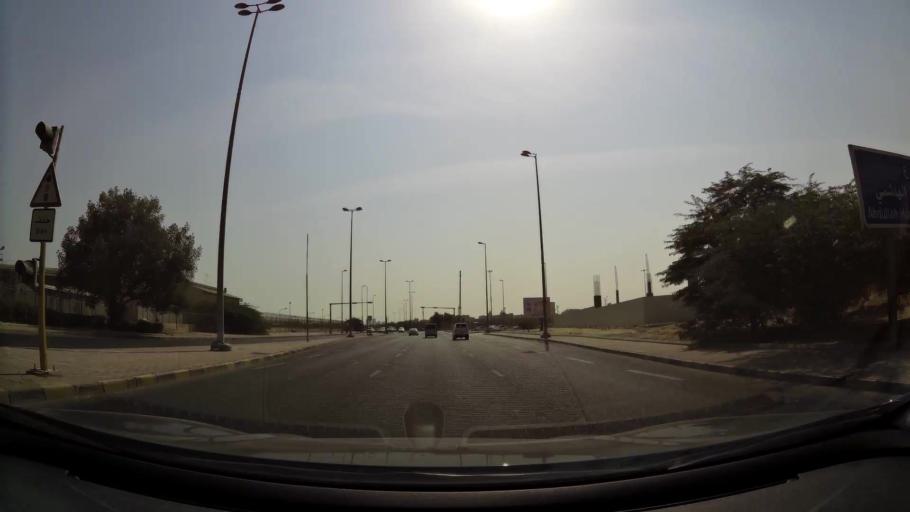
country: KW
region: Al Ahmadi
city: Al Mahbulah
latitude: 29.1220
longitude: 48.1333
